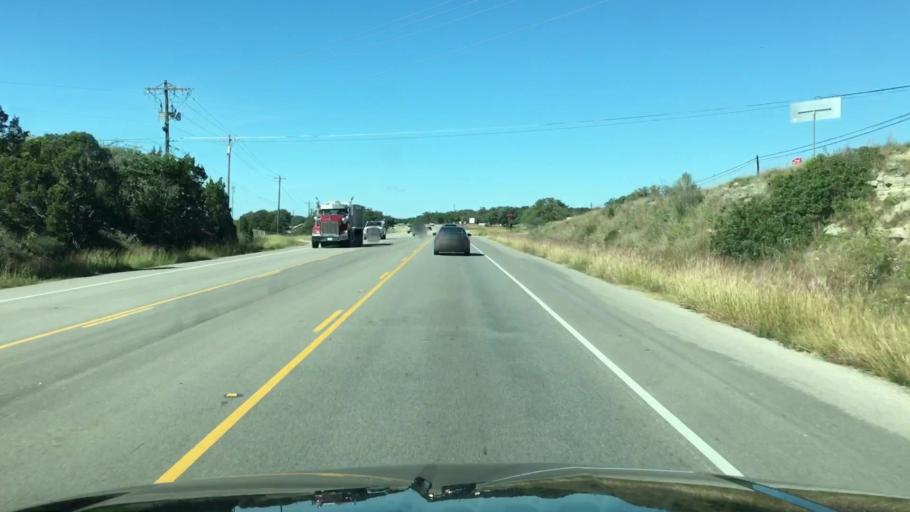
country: US
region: Texas
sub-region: Hays County
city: Dripping Springs
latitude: 30.1983
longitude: -98.1793
